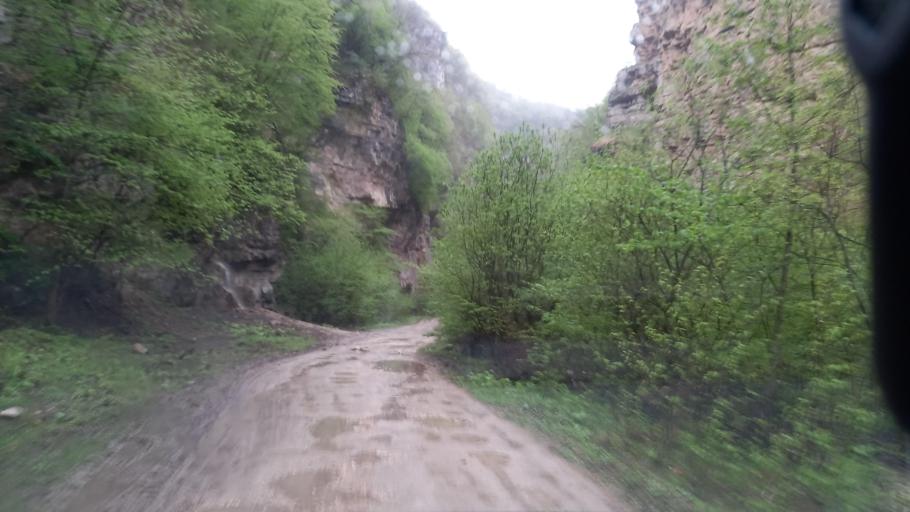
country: RU
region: Kabardino-Balkariya
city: Bylym
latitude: 43.5866
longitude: 43.0156
